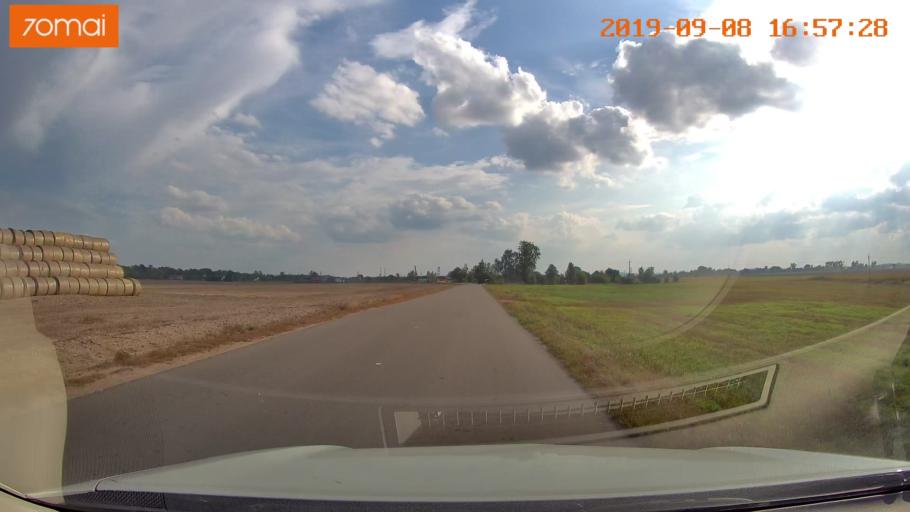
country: BY
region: Grodnenskaya
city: Hrodna
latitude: 53.7325
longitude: 23.9279
